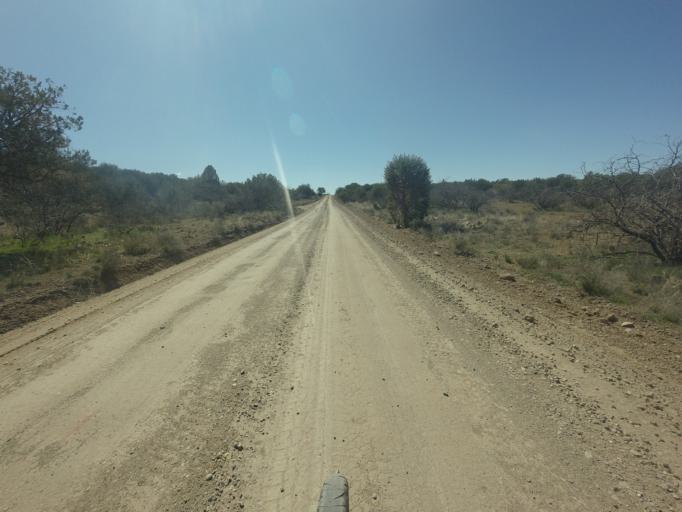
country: US
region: Arizona
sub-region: Yavapai County
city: Lake Montezuma
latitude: 34.6301
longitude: -111.7209
